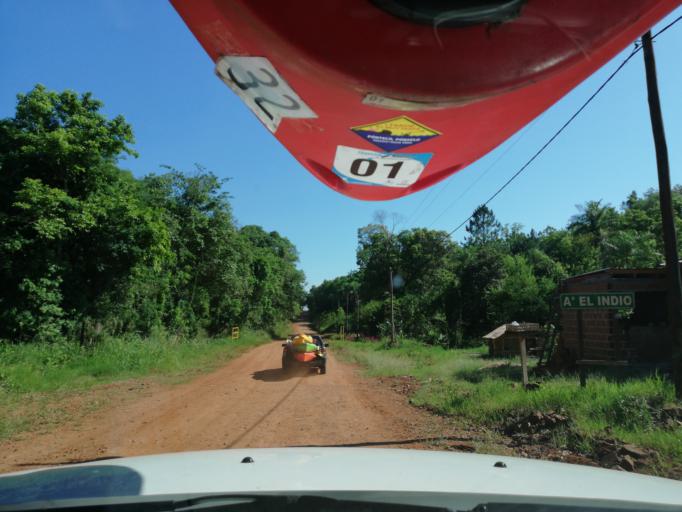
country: AR
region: Misiones
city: Puerto Leoni
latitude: -26.9801
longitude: -55.1647
